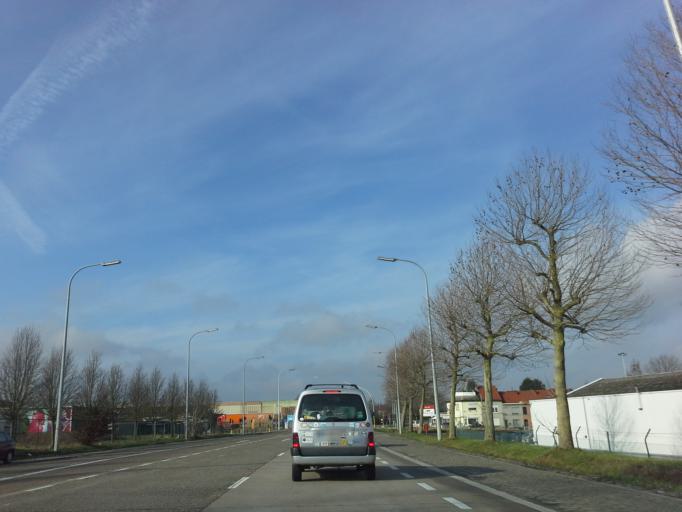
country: BE
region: Flanders
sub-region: Provincie Limburg
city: Sint-Truiden
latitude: 50.8063
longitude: 5.1777
